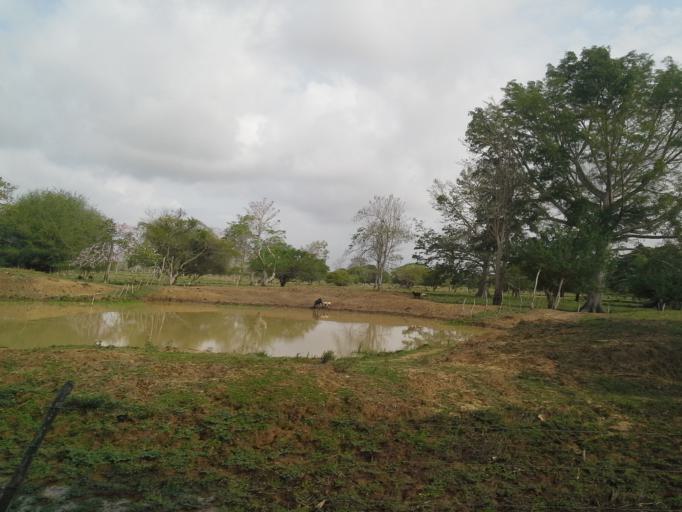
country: CO
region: Cordoba
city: Chima
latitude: 9.1797
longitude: -75.6082
